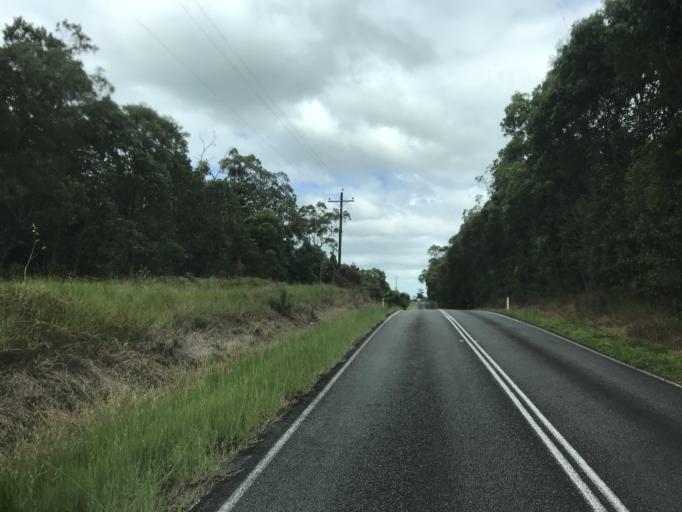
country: AU
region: Queensland
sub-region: Cassowary Coast
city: Innisfail
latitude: -17.8435
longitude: 146.0557
